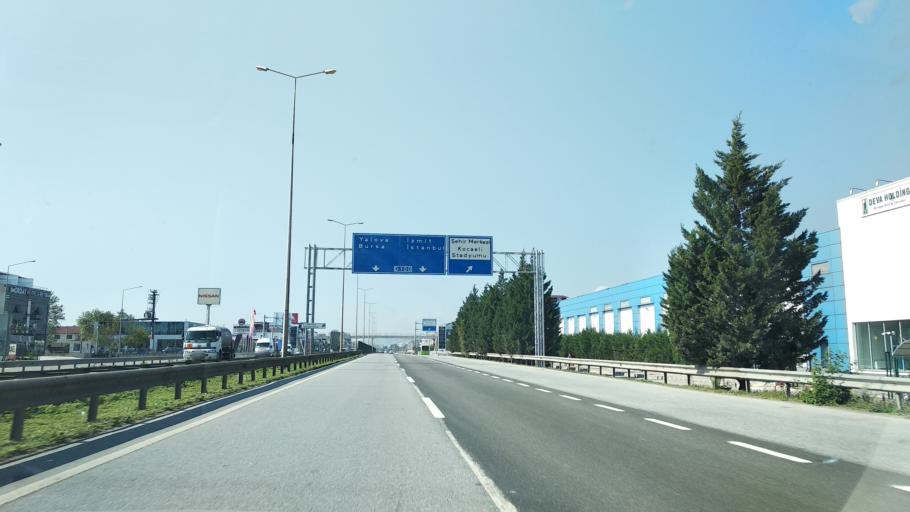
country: TR
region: Kocaeli
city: Kosekoy
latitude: 40.7523
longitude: 30.0317
